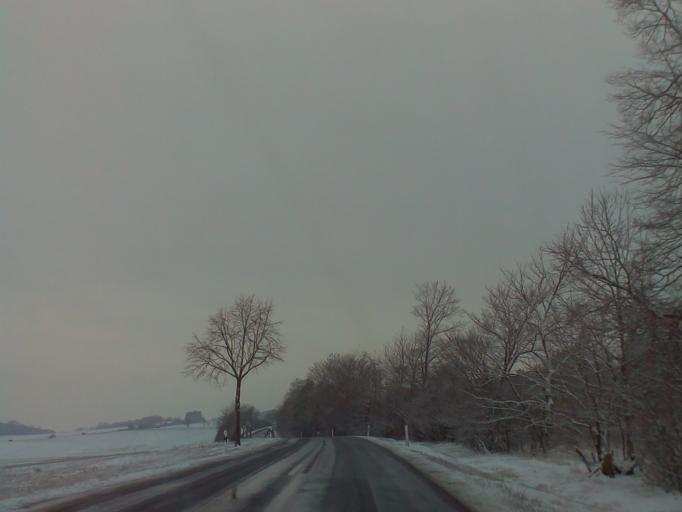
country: DE
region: Thuringia
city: Stadtilm
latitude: 50.7608
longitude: 11.1312
